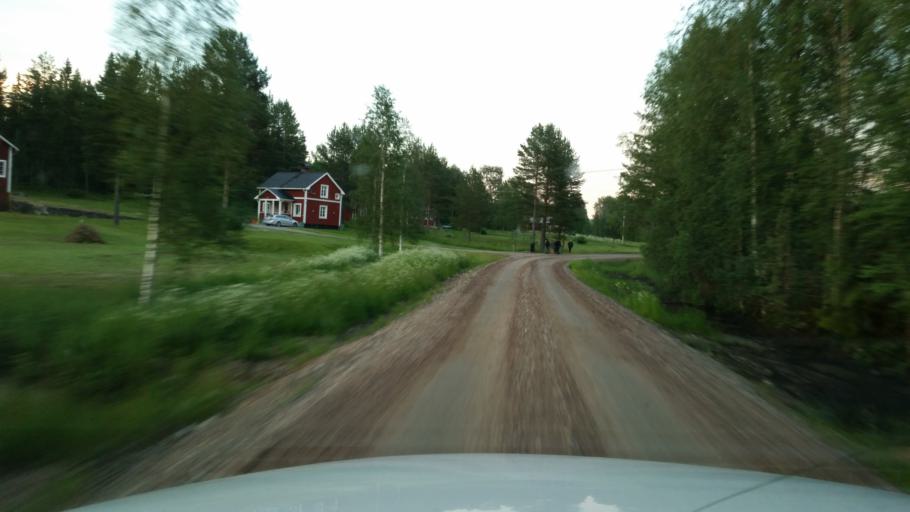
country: SE
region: Vaesternorrland
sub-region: Ange Kommun
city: Ange
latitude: 62.1847
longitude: 15.6344
